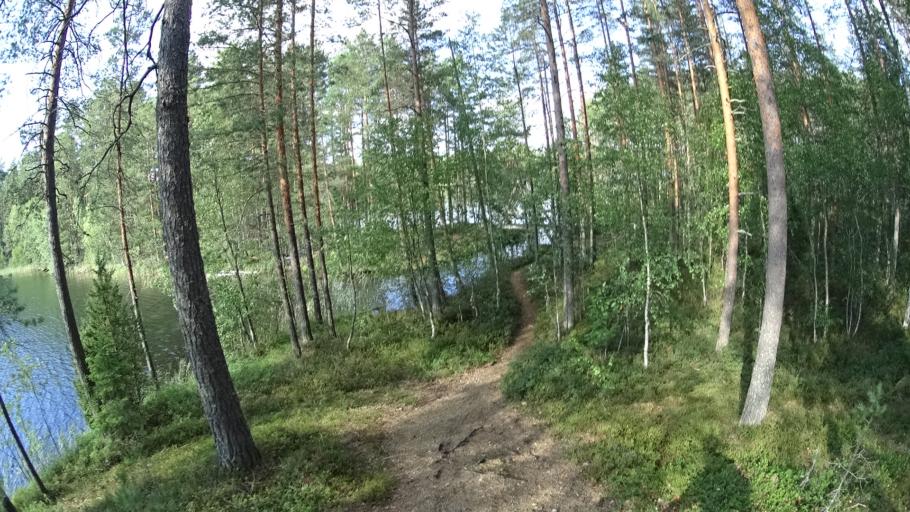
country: FI
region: Uusimaa
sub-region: Helsinki
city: Kaerkoelae
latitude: 60.7358
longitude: 24.0572
